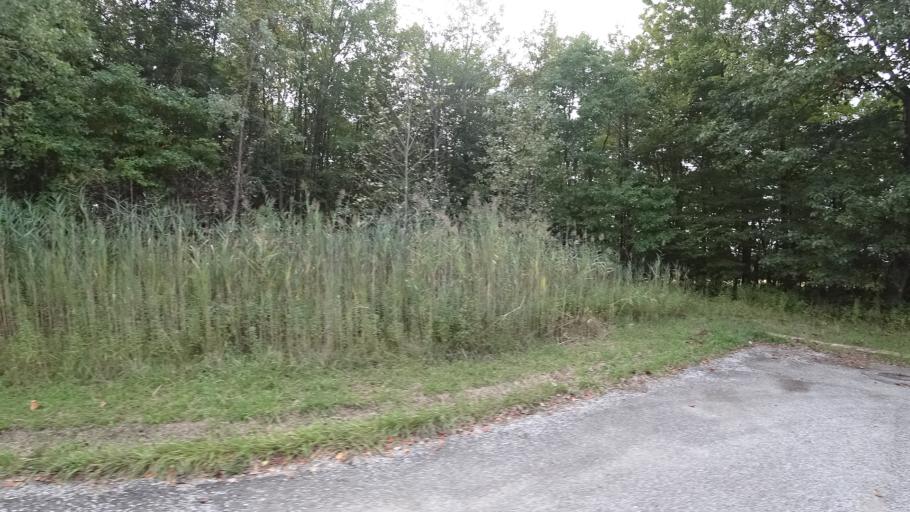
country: US
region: Indiana
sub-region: LaPorte County
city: Long Beach
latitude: 41.7218
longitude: -86.8450
